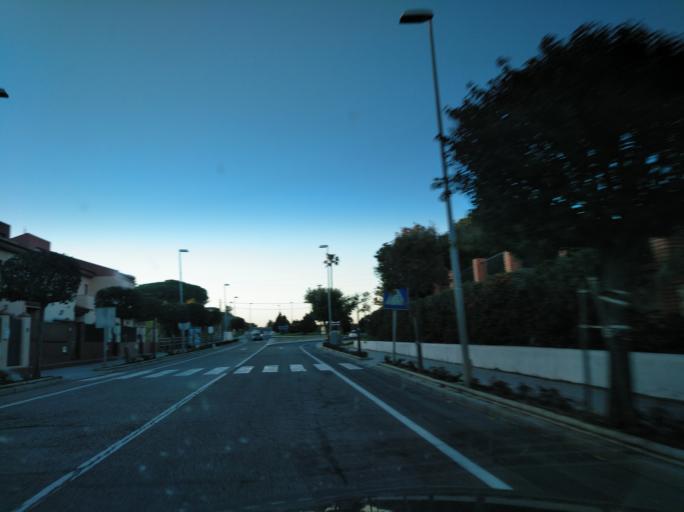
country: ES
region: Andalusia
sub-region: Provincia de Huelva
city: Ayamonte
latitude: 37.2249
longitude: -7.4029
